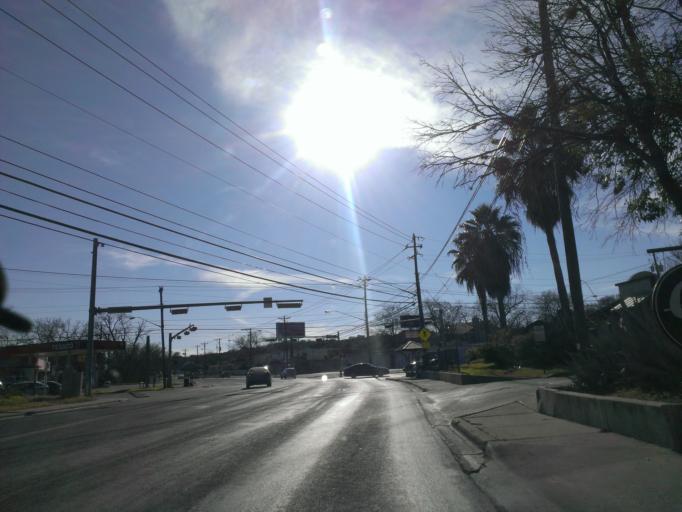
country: US
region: Texas
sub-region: Travis County
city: Austin
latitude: 30.2426
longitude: -97.7591
